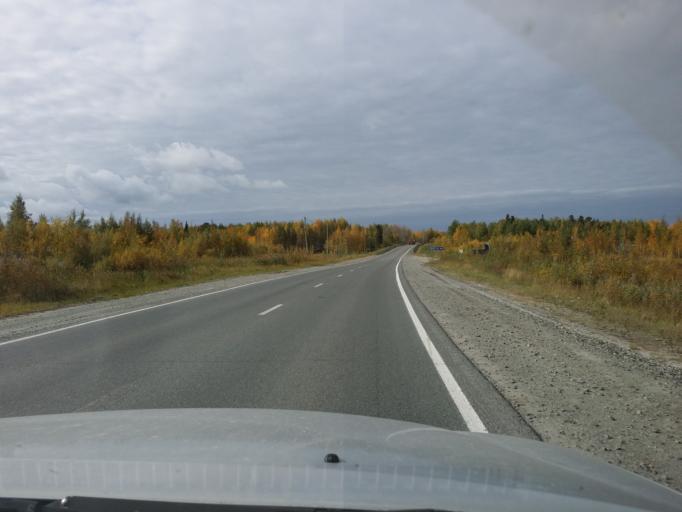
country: RU
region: Khanty-Mansiyskiy Avtonomnyy Okrug
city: Megion
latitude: 61.1053
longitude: 76.0032
